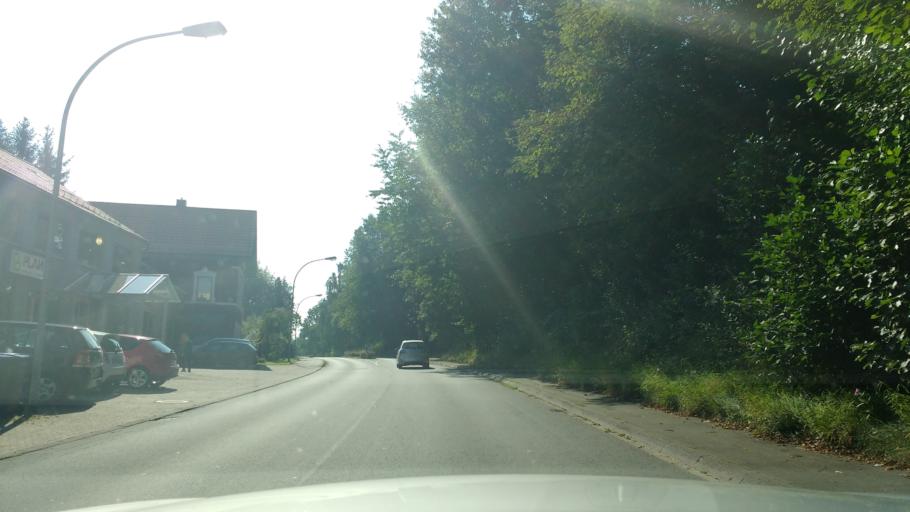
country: DE
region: North Rhine-Westphalia
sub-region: Regierungsbezirk Detmold
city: Dorentrup
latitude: 52.0399
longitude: 9.0027
